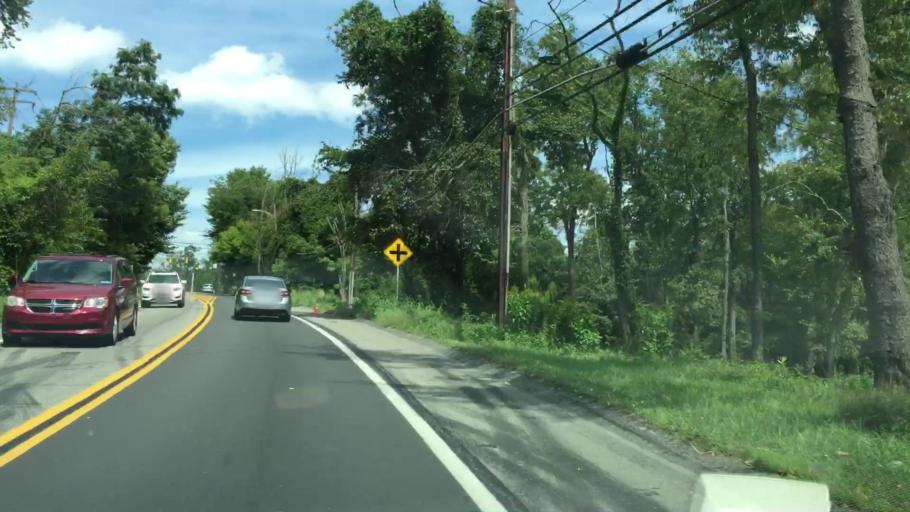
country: US
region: Pennsylvania
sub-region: Allegheny County
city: Bethel Park
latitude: 40.3344
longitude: -80.0201
